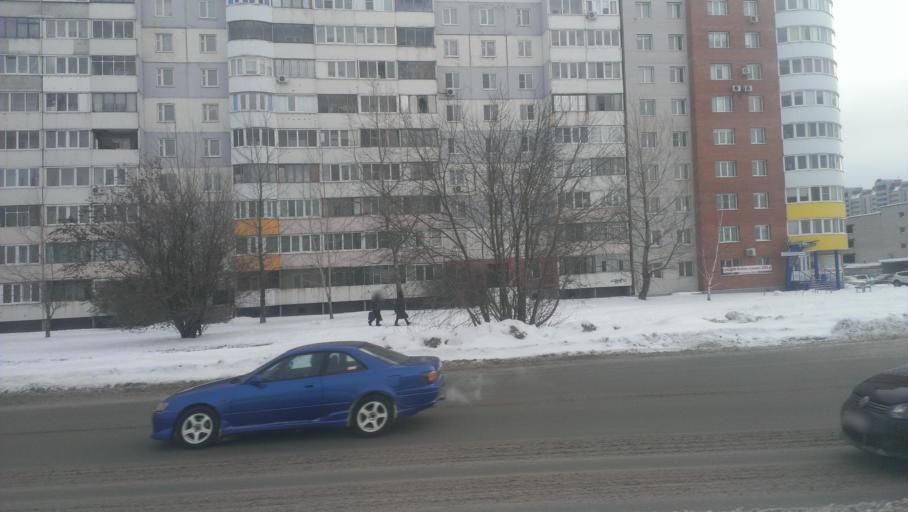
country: RU
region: Altai Krai
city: Novosilikatnyy
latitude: 53.3321
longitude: 83.6682
